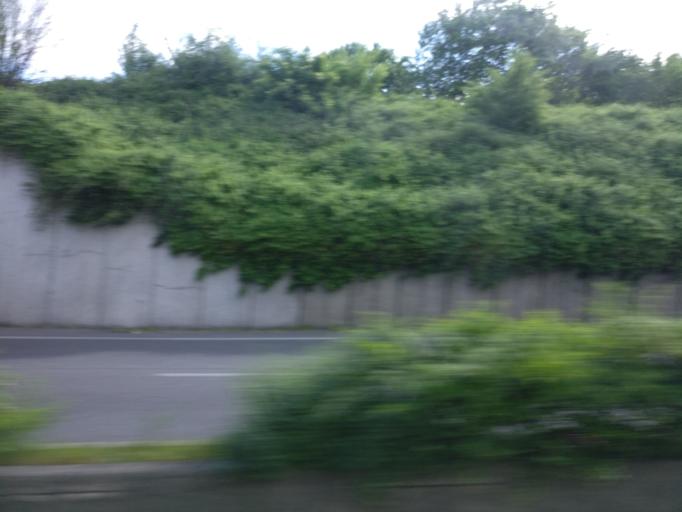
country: IT
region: Lombardy
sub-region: Citta metropolitana di Milano
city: Baranzate
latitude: 45.4926
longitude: 9.1299
